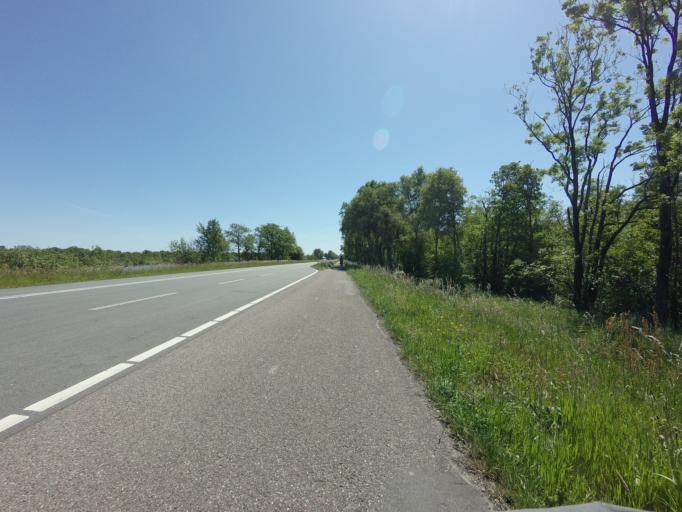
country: NL
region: North Holland
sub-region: Gemeente Wijdemeren
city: Oud-Loosdrecht
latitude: 52.2338
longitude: 5.0643
